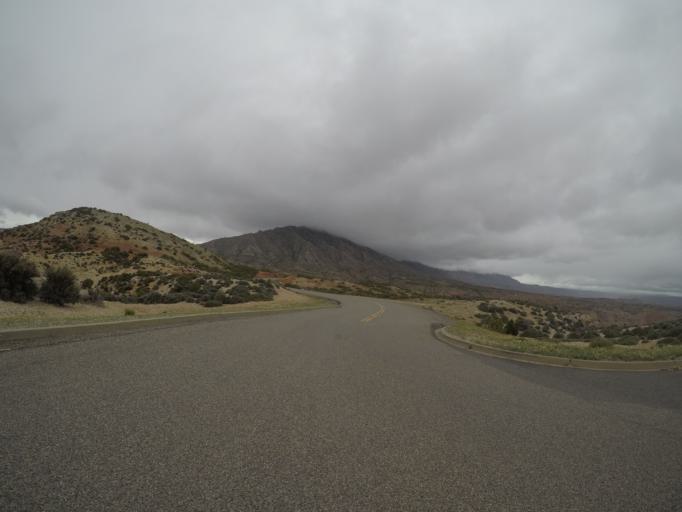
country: US
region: Wyoming
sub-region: Big Horn County
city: Lovell
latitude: 45.0219
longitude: -108.2517
